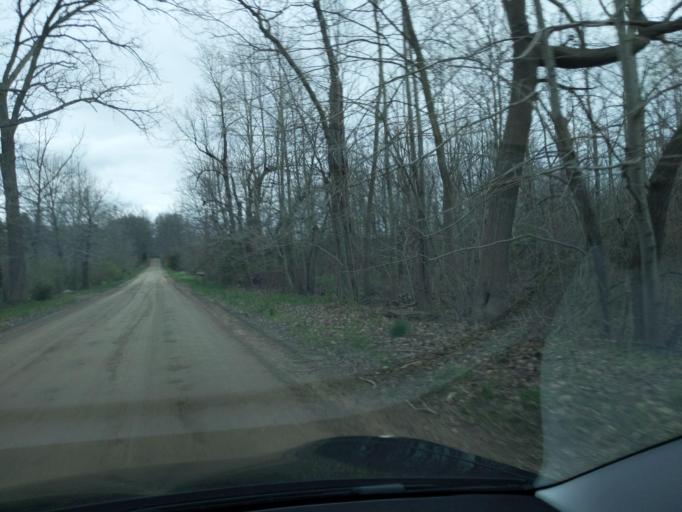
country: US
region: Michigan
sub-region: Ingham County
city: Stockbridge
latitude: 42.4462
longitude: -84.1271
